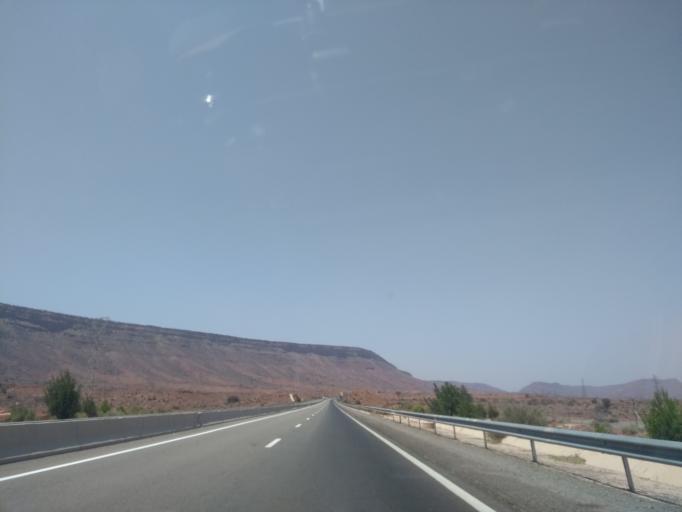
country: MA
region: Marrakech-Tensift-Al Haouz
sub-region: Chichaoua
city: Timezgadiouine
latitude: 30.9141
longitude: -9.0708
